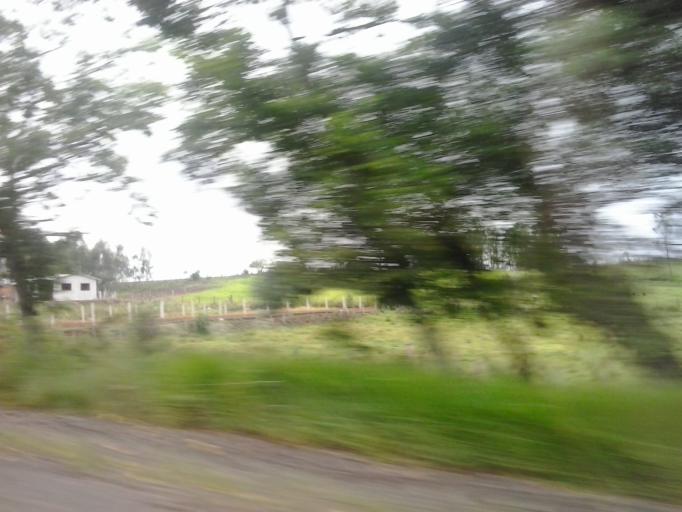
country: BR
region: Rio Grande do Sul
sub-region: Santa Maria
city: Santa Maria
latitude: -29.7229
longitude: -53.3924
